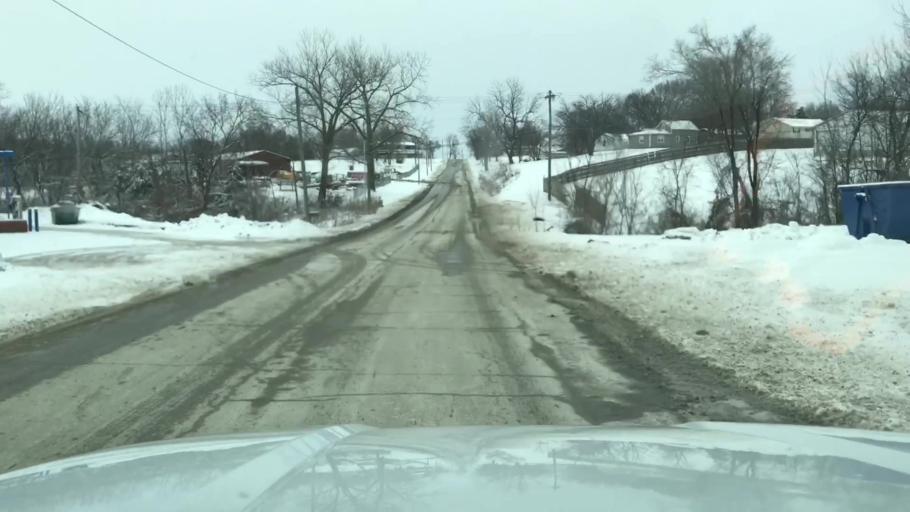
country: US
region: Missouri
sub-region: Clinton County
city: Cameron
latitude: 39.7478
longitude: -94.2332
